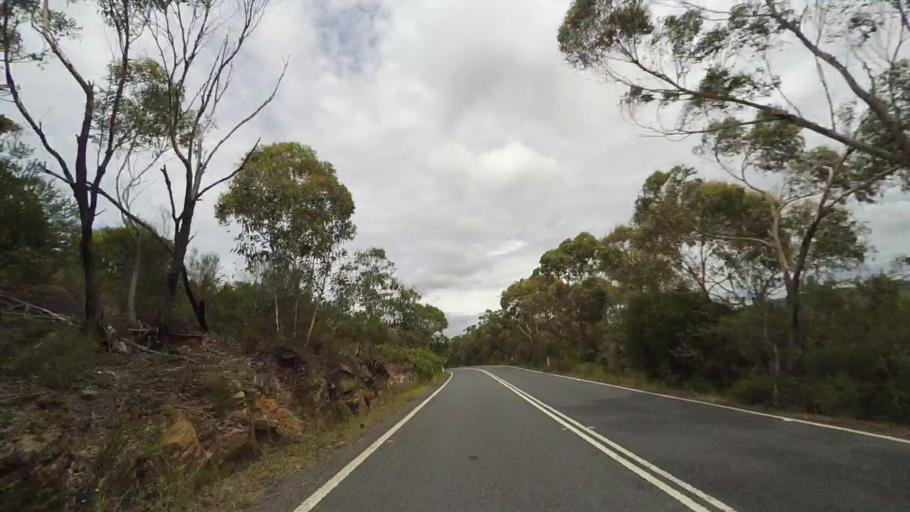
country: AU
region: New South Wales
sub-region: Sutherland Shire
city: Heathcote
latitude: -34.1074
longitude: 151.0603
